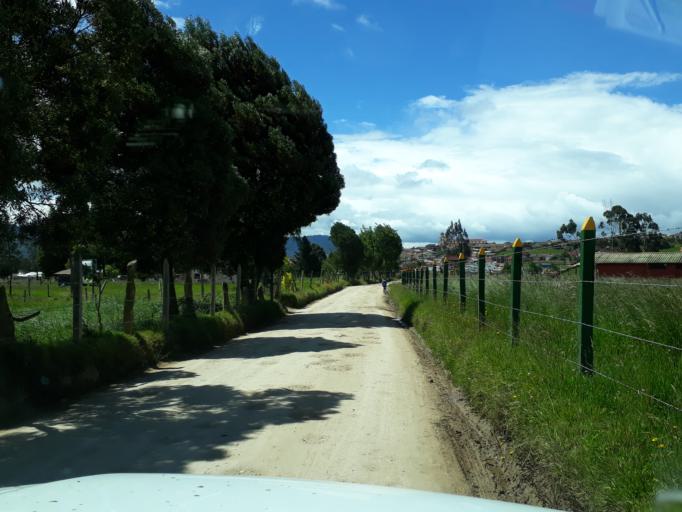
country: CO
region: Cundinamarca
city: Guasca
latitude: 4.8581
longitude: -73.8790
